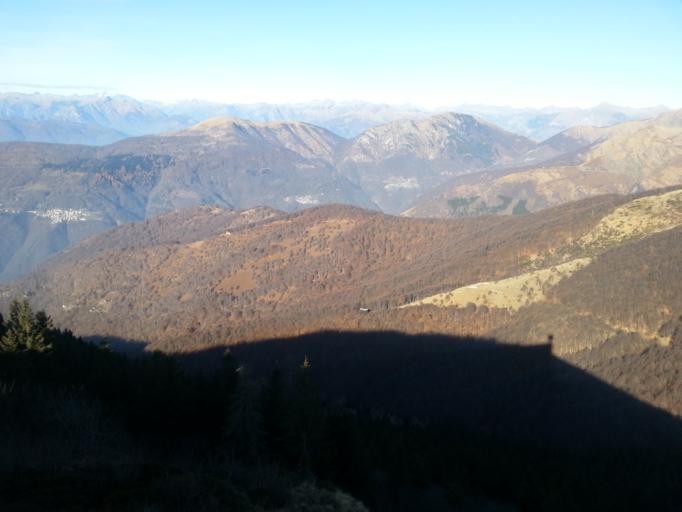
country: IT
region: Lombardy
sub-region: Provincia di Varese
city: Curiglia
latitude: 46.0408
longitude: 8.8333
